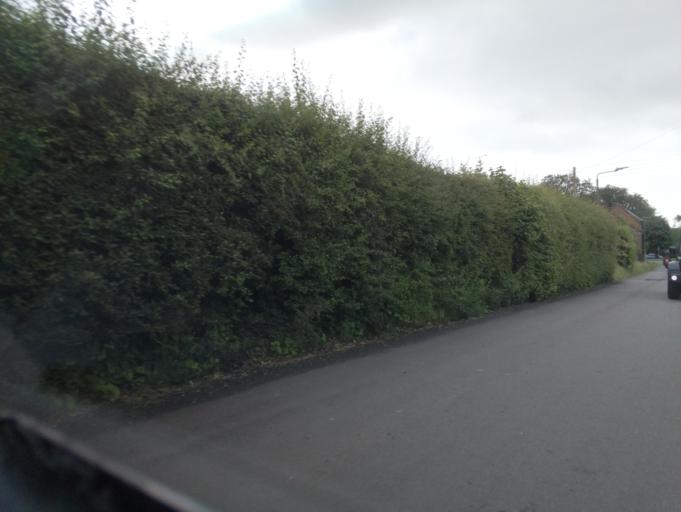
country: GB
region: England
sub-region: Derbyshire
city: Rodsley
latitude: 52.8702
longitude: -1.7154
